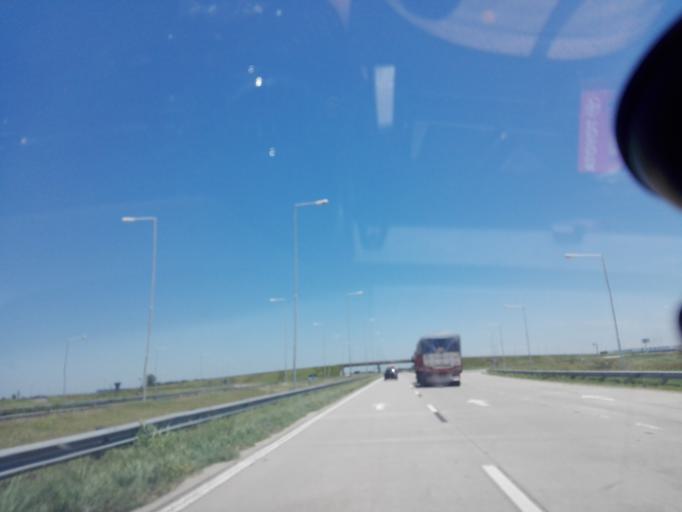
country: AR
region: Cordoba
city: Leones
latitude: -32.5976
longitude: -62.4701
